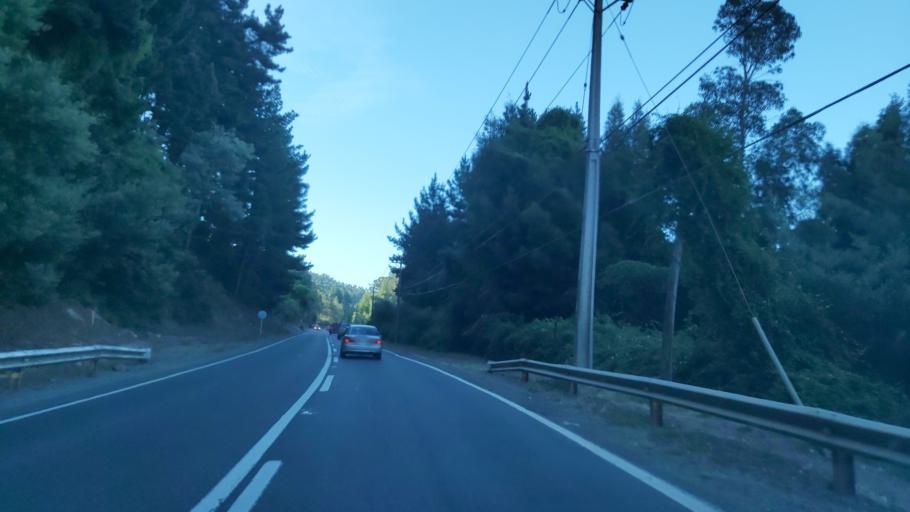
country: CL
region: Biobio
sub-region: Provincia de Concepcion
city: Chiguayante
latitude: -36.8875
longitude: -73.0597
